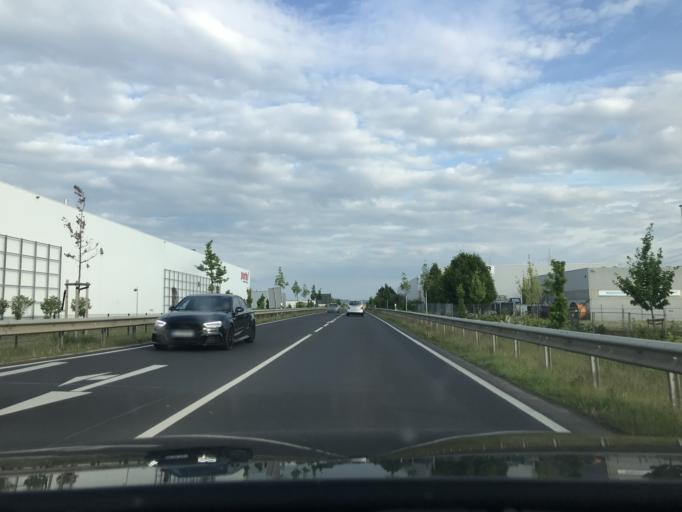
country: DE
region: North Rhine-Westphalia
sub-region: Regierungsbezirk Koln
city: Alfter
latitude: 50.7590
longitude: 7.0239
